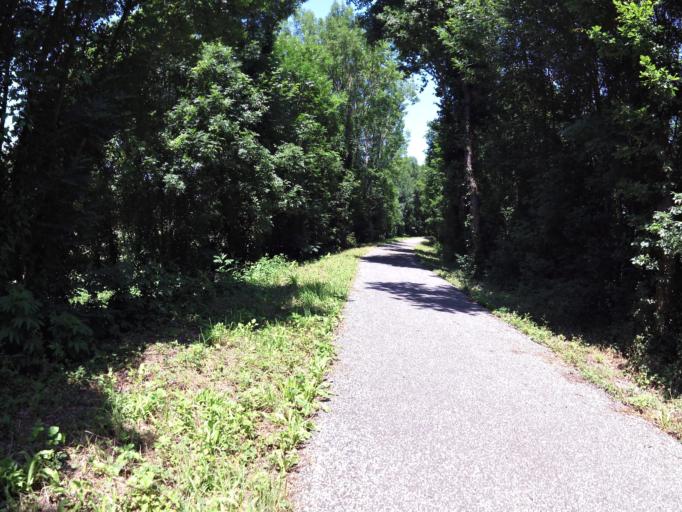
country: FR
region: Aquitaine
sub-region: Departement des Pyrenees-Atlantiques
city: Salies-de-Bearn
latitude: 43.4481
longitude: -0.9946
